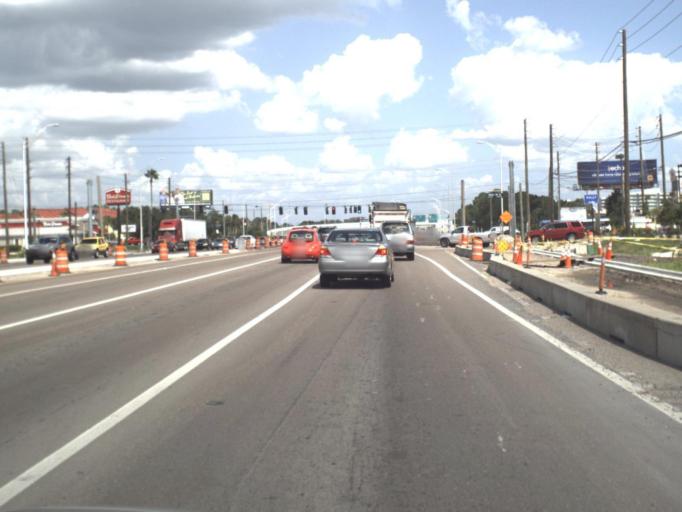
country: US
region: Florida
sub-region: Pinellas County
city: Feather Sound
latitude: 27.8937
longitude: -82.6813
